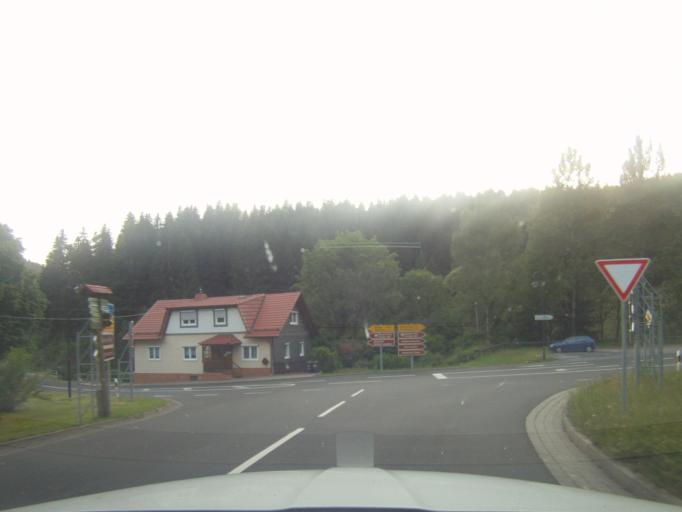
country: DE
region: Thuringia
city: Eisfeld
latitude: 50.4867
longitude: 10.9078
